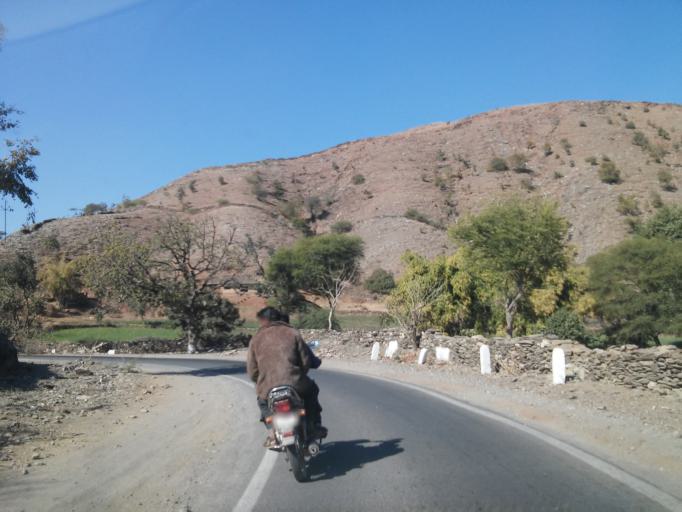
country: IN
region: Rajasthan
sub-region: Udaipur
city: Udaipur
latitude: 24.4994
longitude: 73.6075
